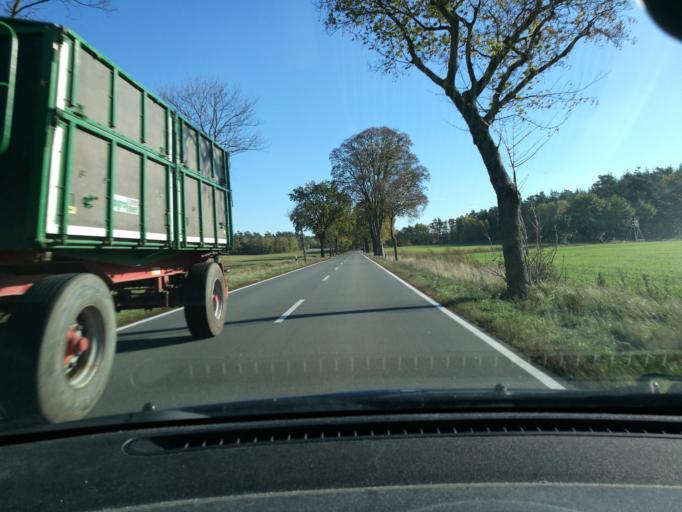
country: DE
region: Lower Saxony
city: Nahrendorf
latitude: 53.1556
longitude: 10.8200
